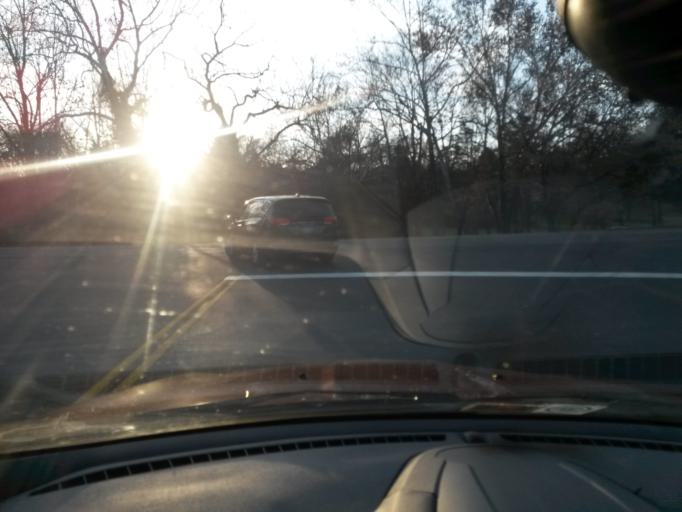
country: US
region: Virginia
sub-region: Roanoke County
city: Hollins
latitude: 37.3374
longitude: -79.9687
